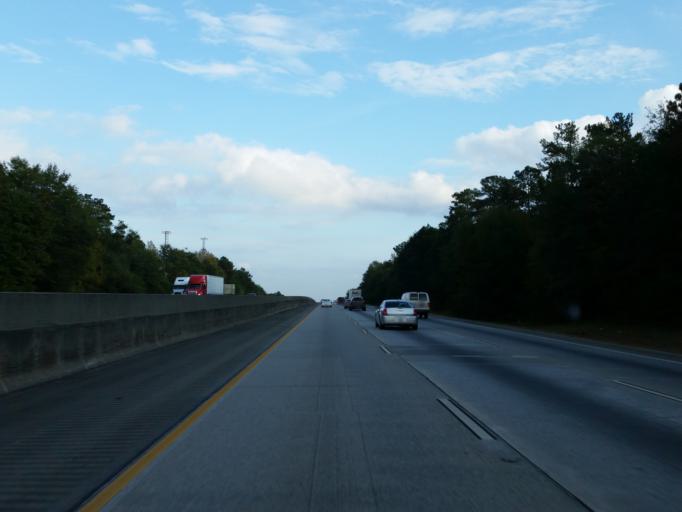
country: US
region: Georgia
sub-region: Monroe County
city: Forsyth
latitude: 33.0150
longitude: -83.8856
